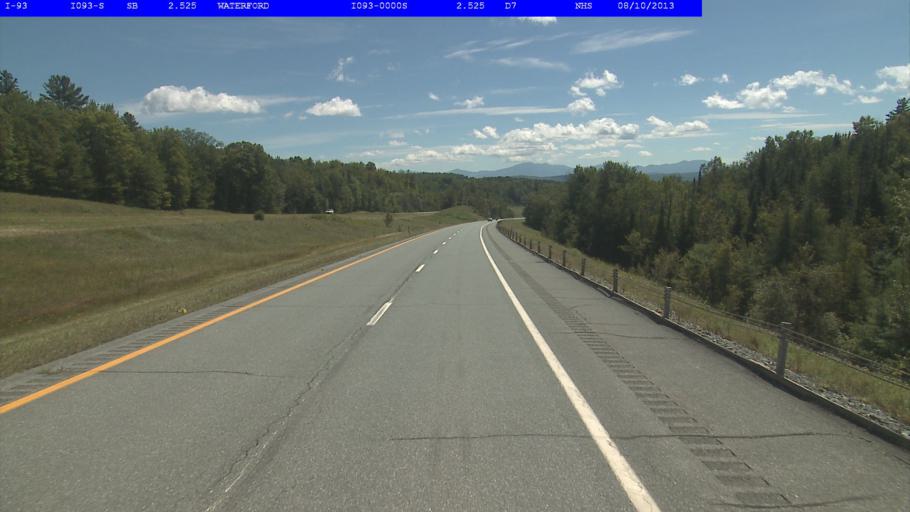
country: US
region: Vermont
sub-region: Caledonia County
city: Saint Johnsbury
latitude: 44.3760
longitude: -71.9124
